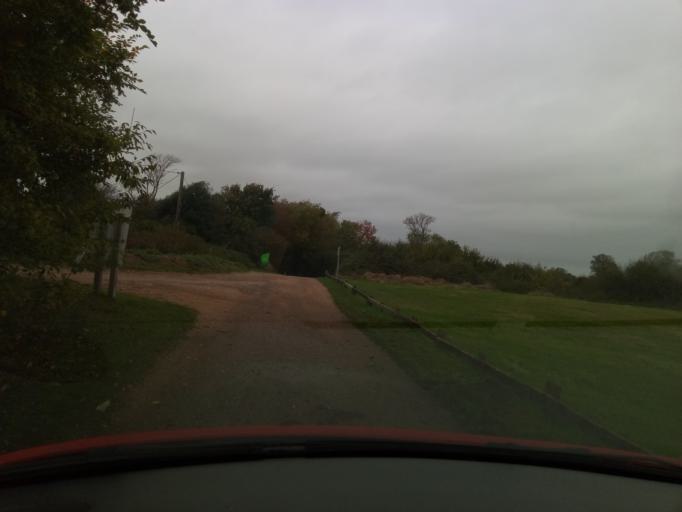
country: GB
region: England
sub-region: Essex
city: Brightlingsea
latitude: 51.7926
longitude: 0.9932
